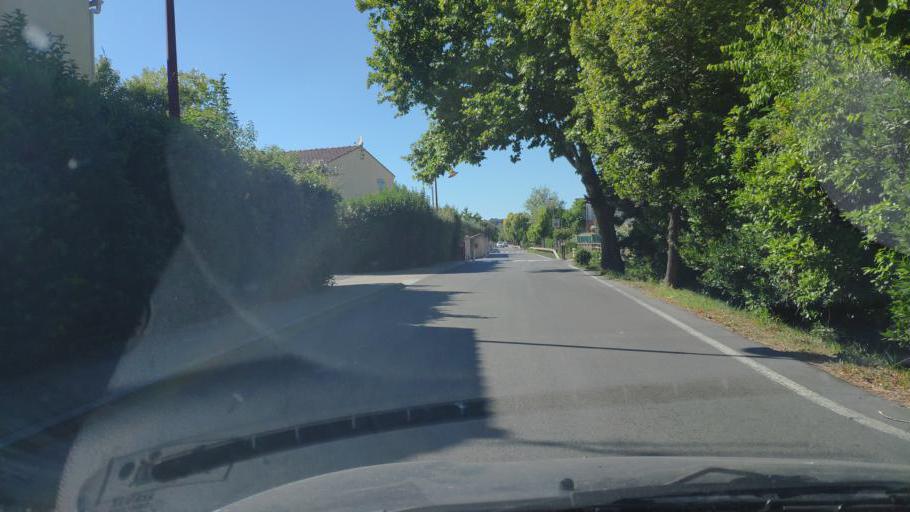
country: FR
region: Provence-Alpes-Cote d'Azur
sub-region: Departement du Vaucluse
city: Entraigues-sur-la-Sorgue
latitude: 44.0018
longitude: 4.9198
